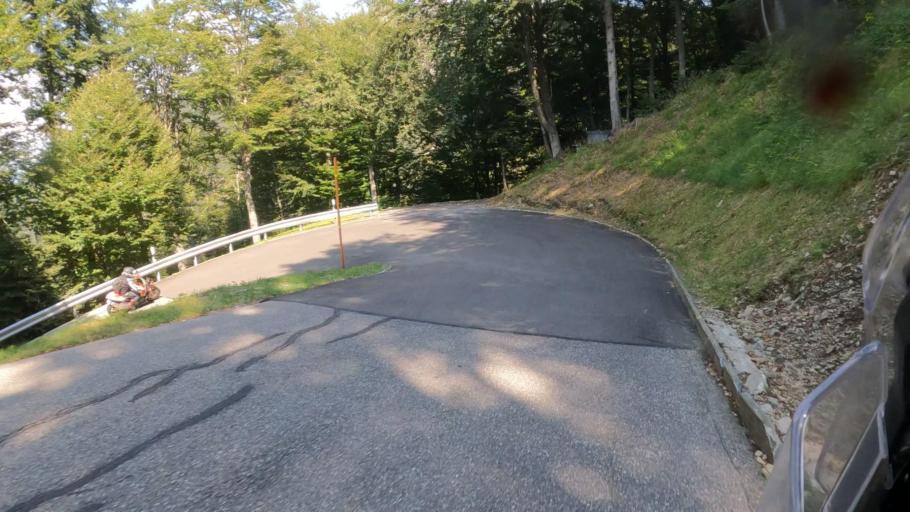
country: CH
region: Ticino
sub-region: Locarno District
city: Magadino
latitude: 46.1135
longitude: 8.8497
